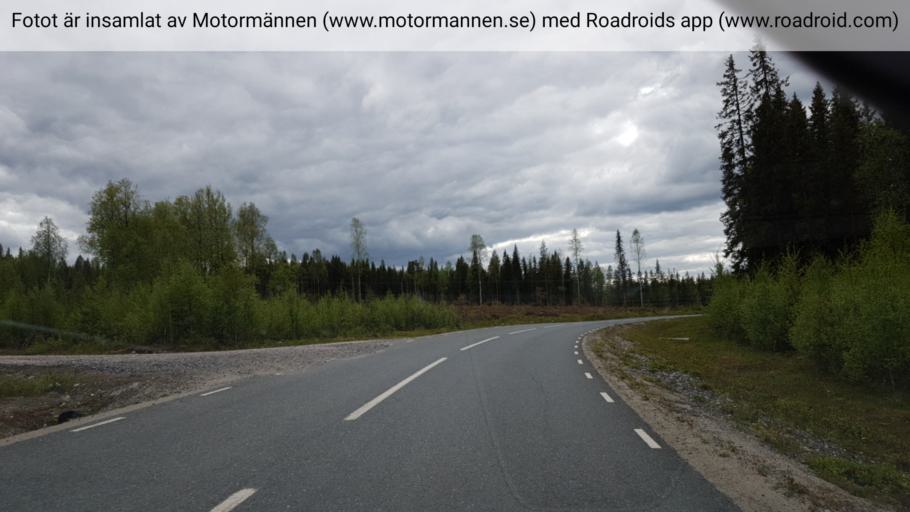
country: SE
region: Vaesterbotten
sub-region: Vindelns Kommun
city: Vindeln
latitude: 64.4837
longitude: 19.7750
